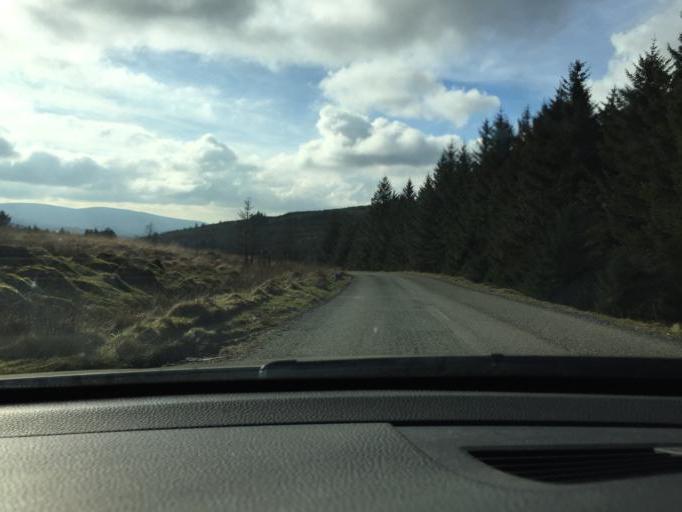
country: IE
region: Leinster
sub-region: Wicklow
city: Valleymount
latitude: 53.0570
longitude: -6.4158
